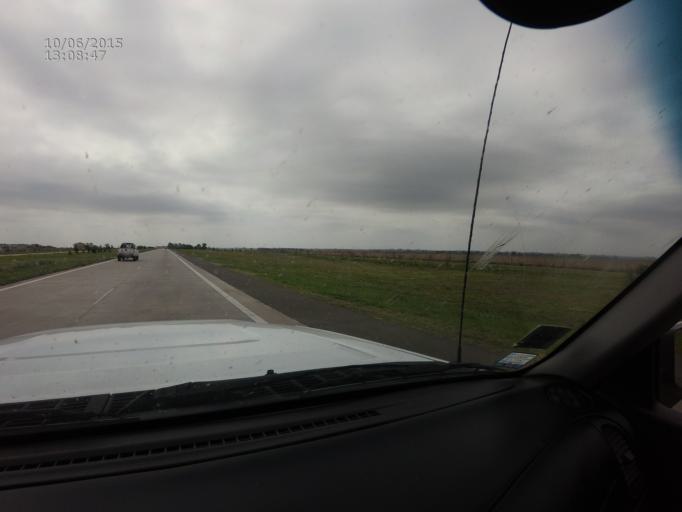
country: AR
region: Cordoba
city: General Roca
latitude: -32.7553
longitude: -61.8607
